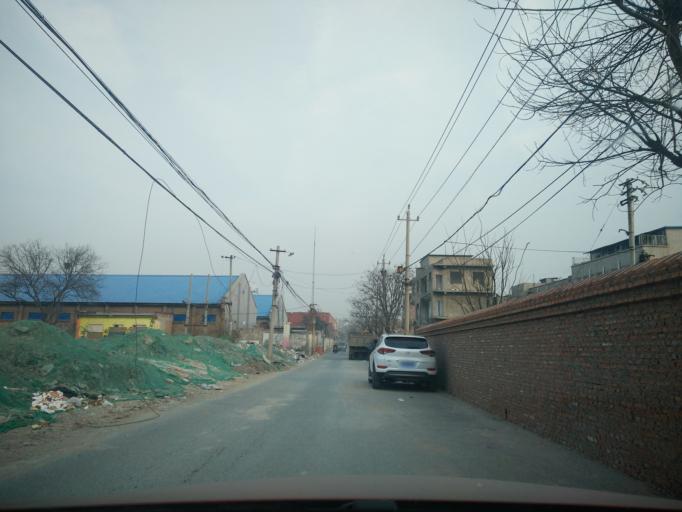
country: CN
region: Beijing
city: Jiugong
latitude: 39.8010
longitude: 116.4294
